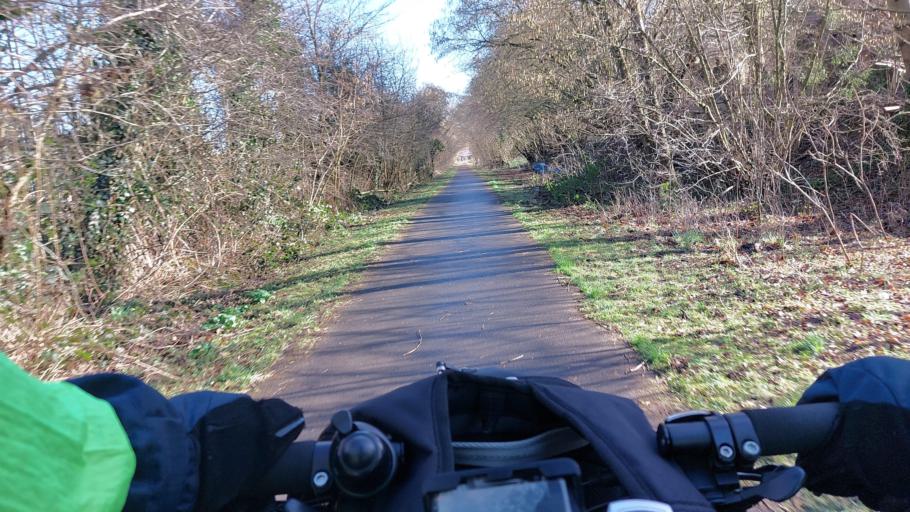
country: BE
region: Wallonia
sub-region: Province du Brabant Wallon
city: Ittre
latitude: 50.6061
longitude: 4.2165
